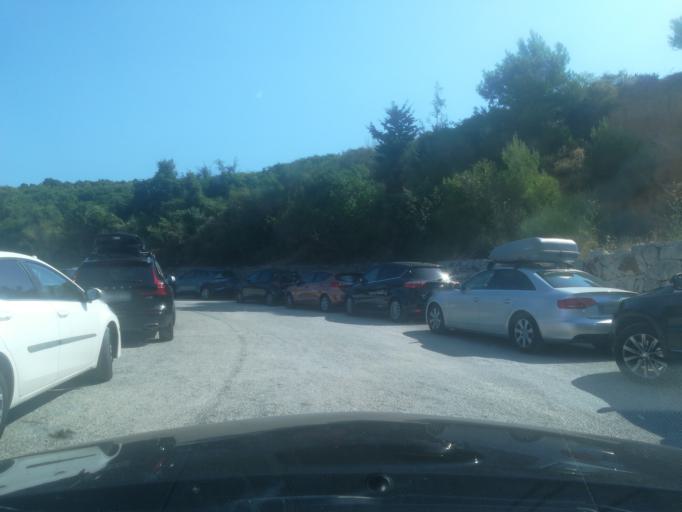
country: HR
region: Primorsko-Goranska
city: Banjol
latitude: 44.7073
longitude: 14.8318
